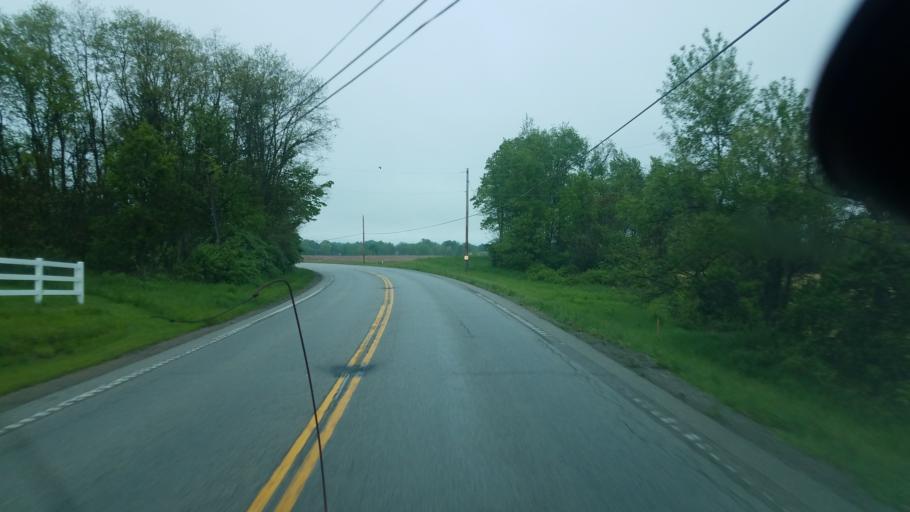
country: US
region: Ohio
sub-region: Highland County
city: Hillsboro
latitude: 39.2755
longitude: -83.5940
